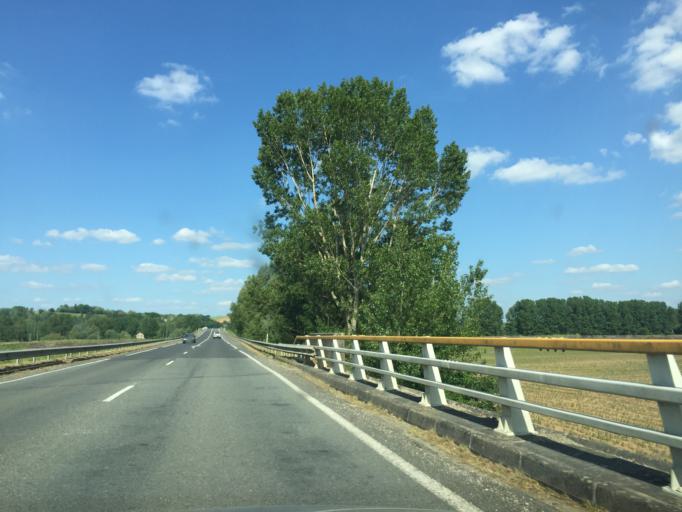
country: FR
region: Aquitaine
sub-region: Departement de la Gironde
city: La Reole
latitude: 44.5696
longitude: -0.0263
